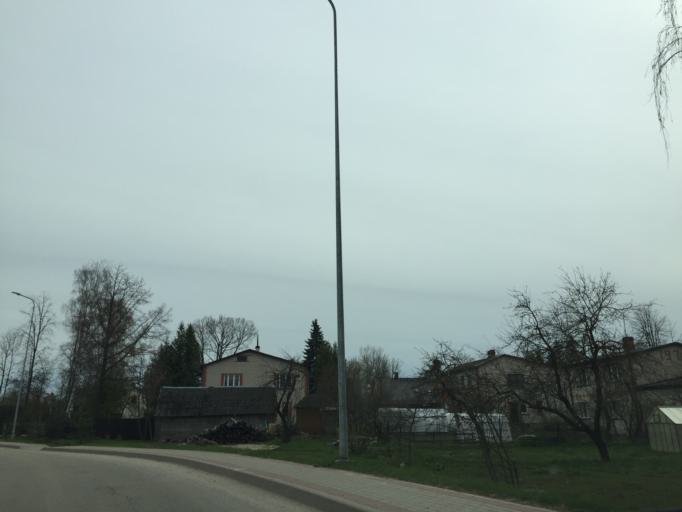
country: LV
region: Ludzas Rajons
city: Ludza
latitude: 56.5614
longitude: 27.7224
